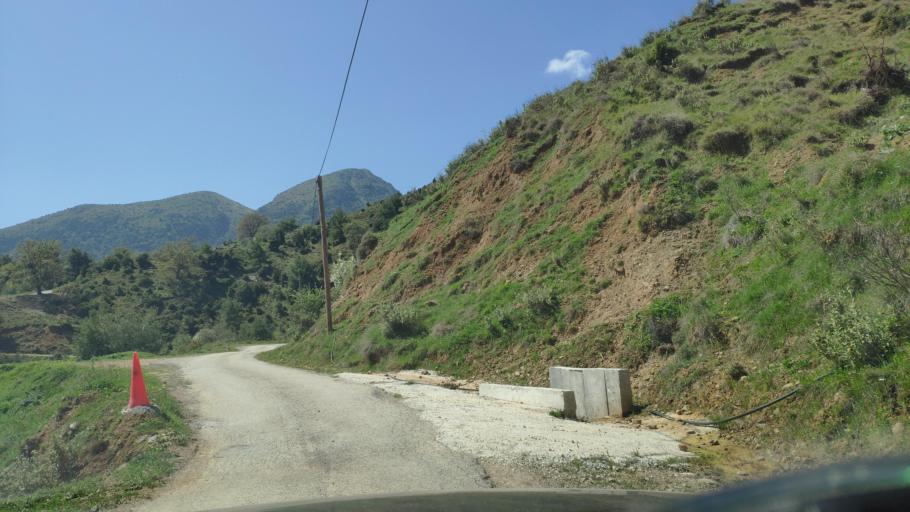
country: GR
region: West Greece
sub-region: Nomos Achaias
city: Akrata
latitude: 38.0827
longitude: 22.3228
